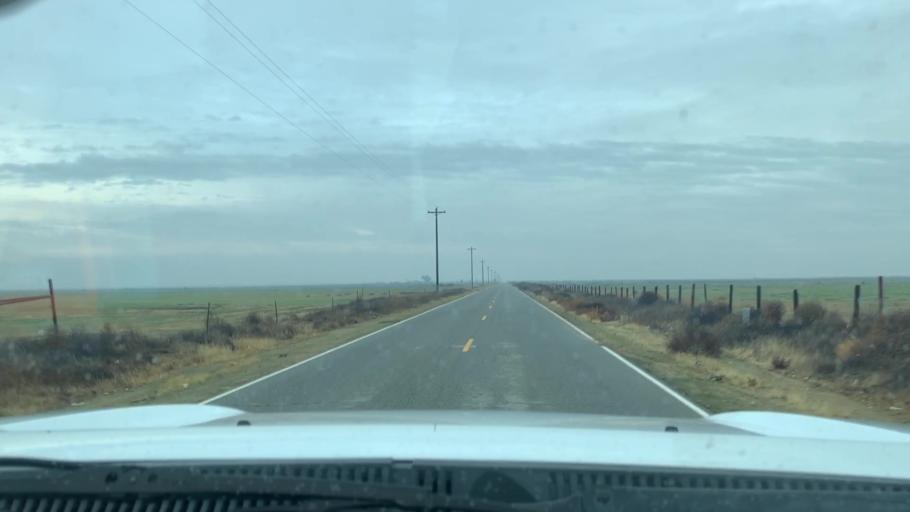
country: US
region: California
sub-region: Kern County
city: Lost Hills
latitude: 35.6884
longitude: -119.5797
